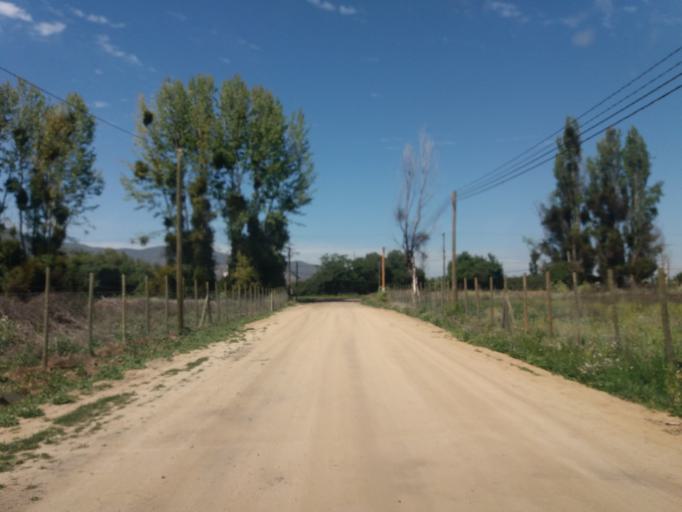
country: CL
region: Valparaiso
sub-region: Provincia de Quillota
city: Quillota
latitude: -32.8775
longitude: -71.2166
